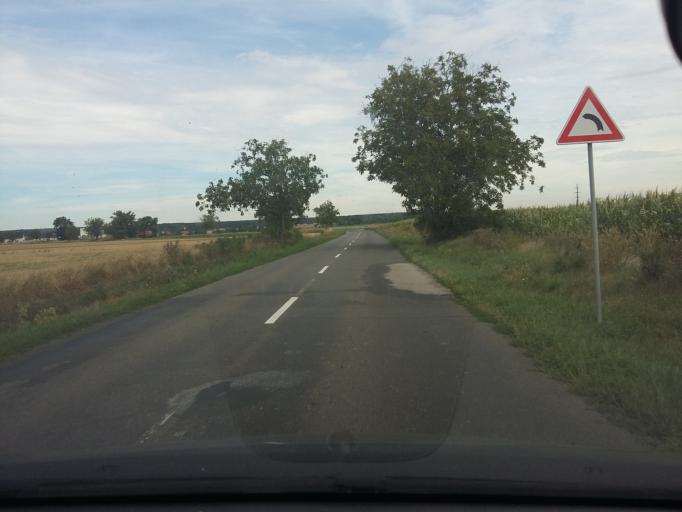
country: SK
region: Bratislavsky
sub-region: Okres Pezinok
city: Pezinok
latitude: 48.2603
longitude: 17.2953
